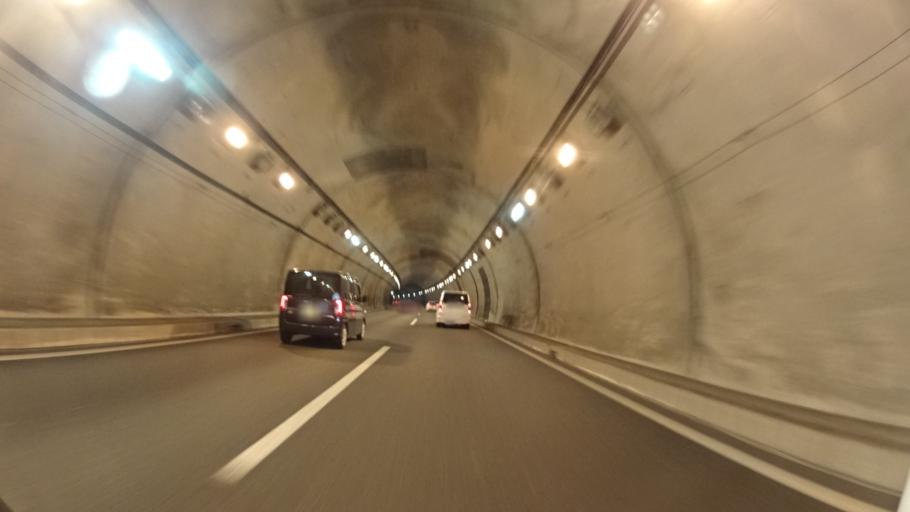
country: JP
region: Ehime
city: Saijo
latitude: 33.8853
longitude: 133.1904
